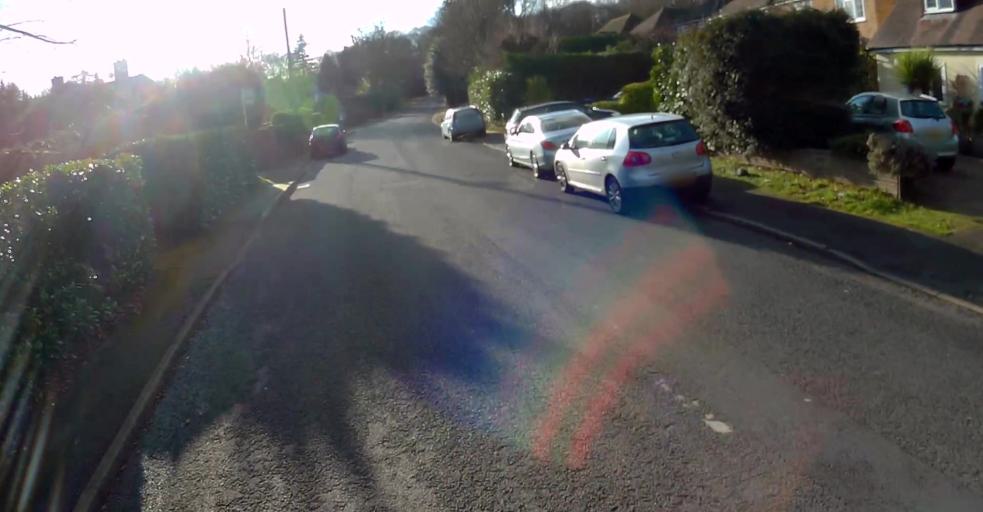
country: GB
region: England
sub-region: Surrey
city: Ottershaw
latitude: 51.3572
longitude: -0.5329
